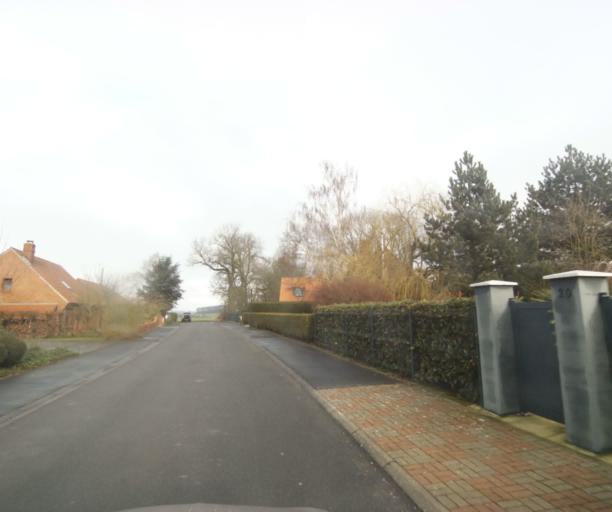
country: FR
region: Nord-Pas-de-Calais
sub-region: Departement du Nord
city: Famars
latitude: 50.2934
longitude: 3.5122
